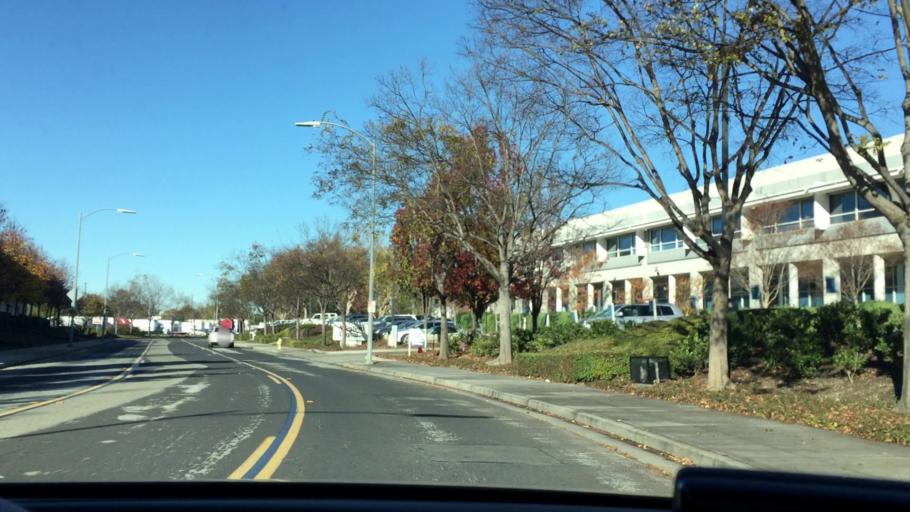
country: US
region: California
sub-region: Santa Clara County
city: Milpitas
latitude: 37.3910
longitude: -121.8838
